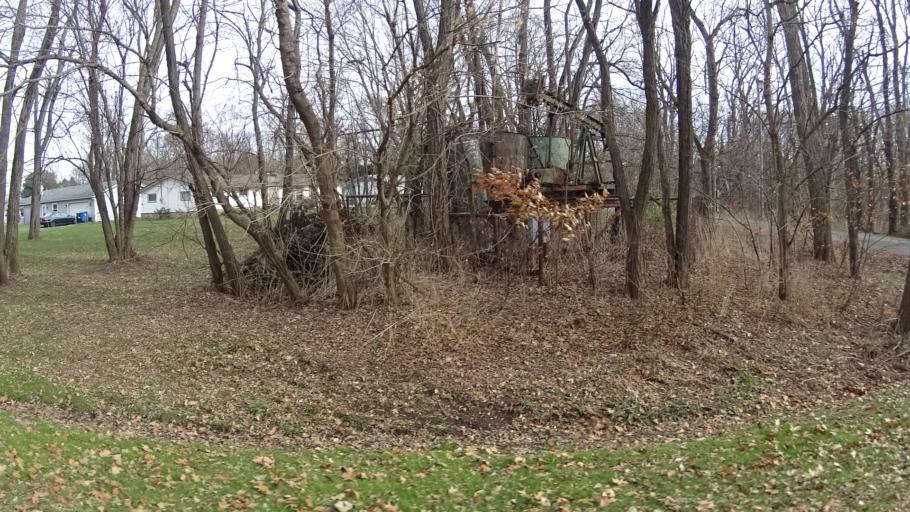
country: US
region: Ohio
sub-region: Cuyahoga County
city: Olmsted Falls
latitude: 41.2993
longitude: -81.9232
